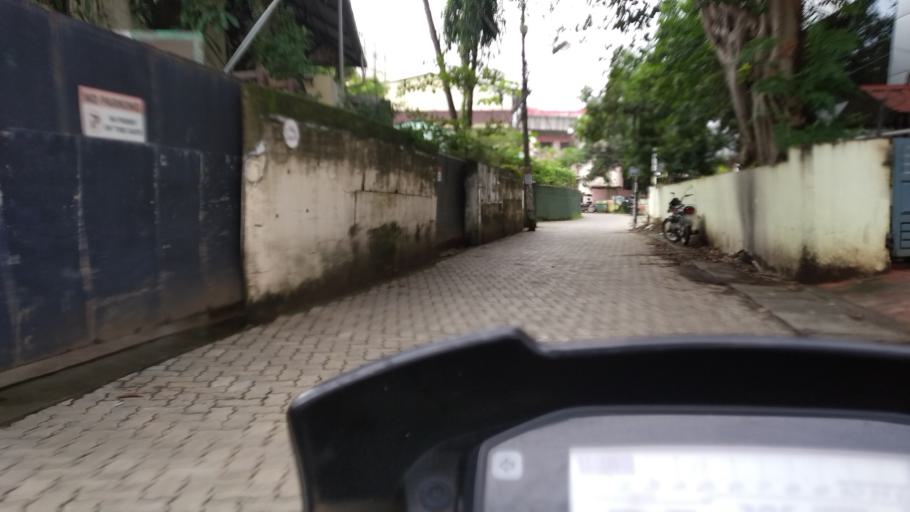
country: IN
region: Kerala
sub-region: Ernakulam
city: Cochin
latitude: 9.9950
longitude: 76.2934
